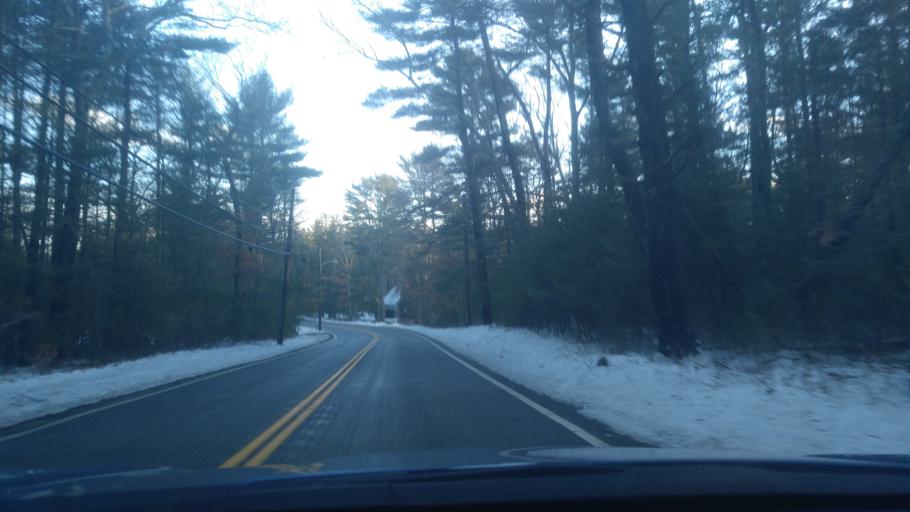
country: US
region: Rhode Island
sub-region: Kent County
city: West Greenwich
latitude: 41.6817
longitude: -71.6160
